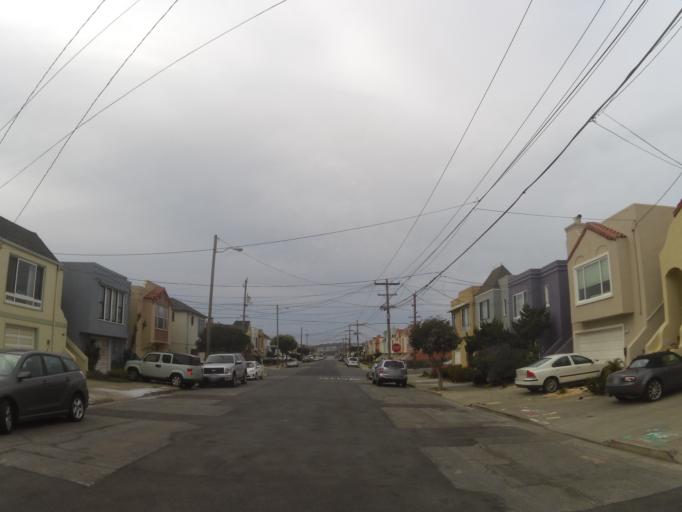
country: US
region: California
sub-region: San Mateo County
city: Daly City
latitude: 37.7468
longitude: -122.5061
